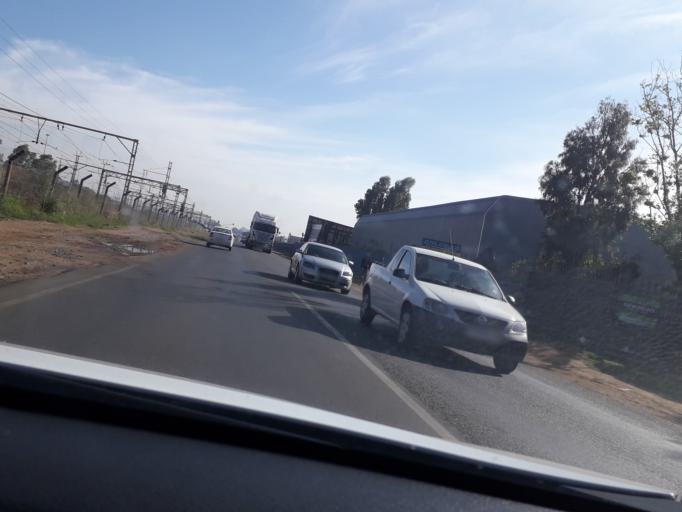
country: ZA
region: Gauteng
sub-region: Ekurhuleni Metropolitan Municipality
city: Boksburg
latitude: -26.1609
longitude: 28.2094
